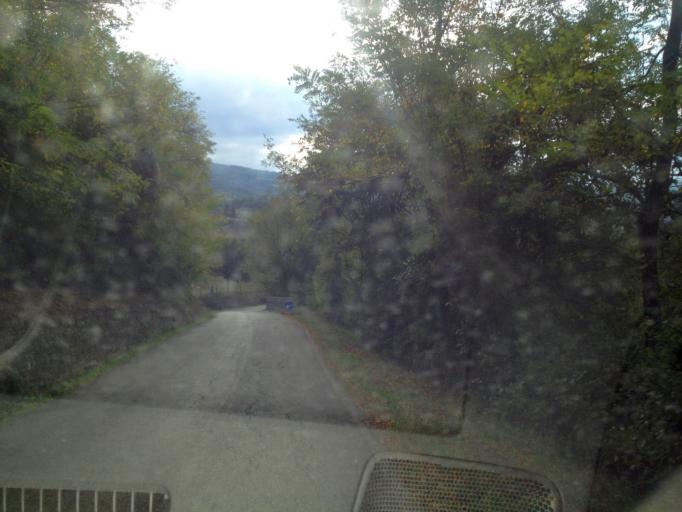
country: IT
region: Tuscany
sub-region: Province of Florence
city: Montebonello
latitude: 43.8529
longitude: 11.4979
